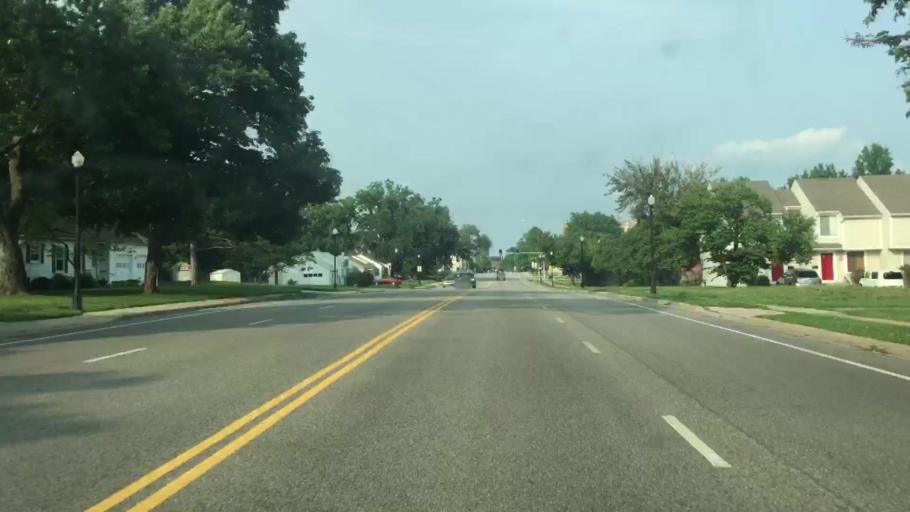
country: US
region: Kansas
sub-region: Johnson County
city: Overland Park
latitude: 38.9782
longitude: -94.6789
